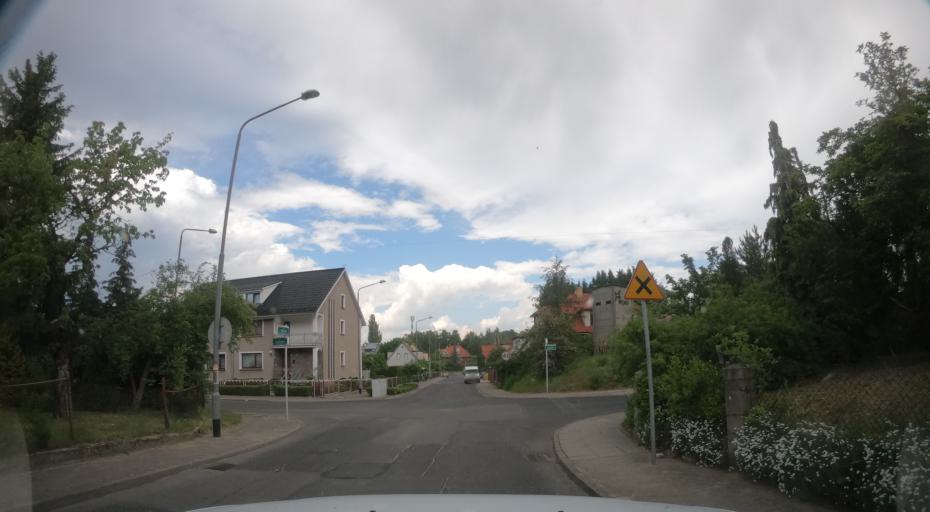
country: PL
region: West Pomeranian Voivodeship
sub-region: Szczecin
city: Szczecin
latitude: 53.3627
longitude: 14.6060
